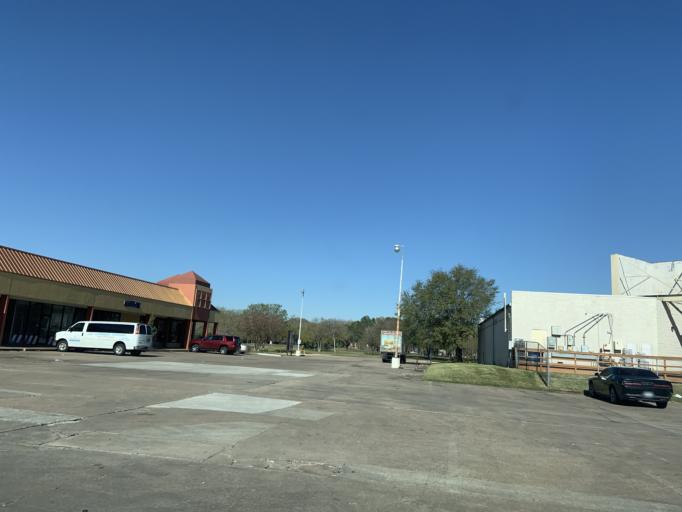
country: US
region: Texas
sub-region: Harris County
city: Bellaire
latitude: 29.6747
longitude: -95.5093
